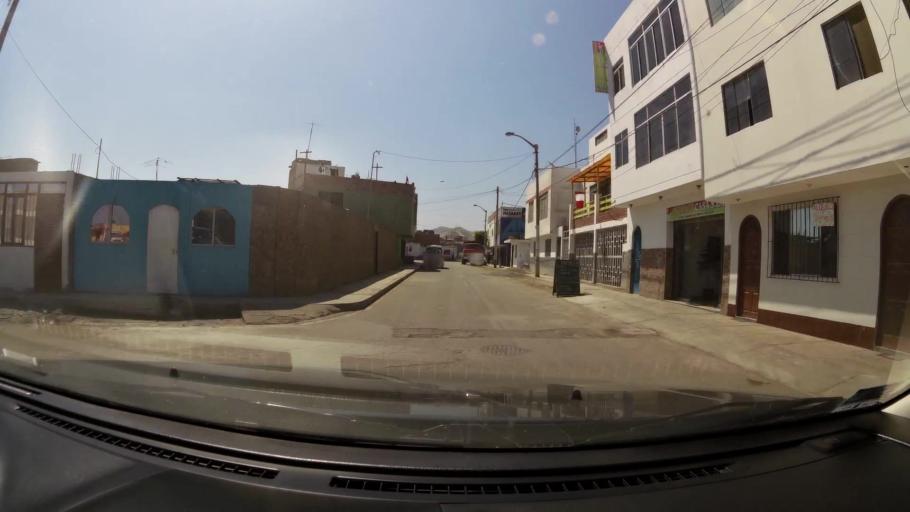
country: PE
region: Lima
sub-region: Provincia de Canete
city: San Vicente de Canete
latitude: -13.0247
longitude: -76.4774
